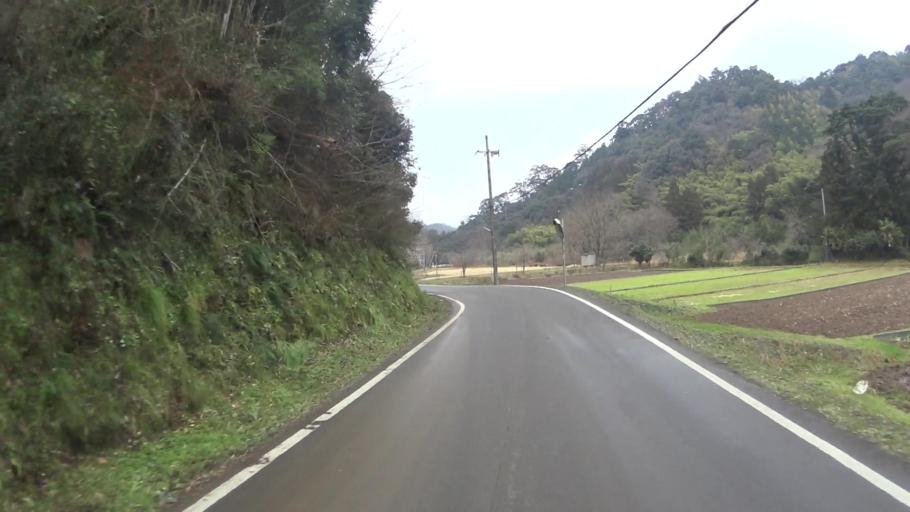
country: JP
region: Kyoto
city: Maizuru
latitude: 35.4249
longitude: 135.2986
